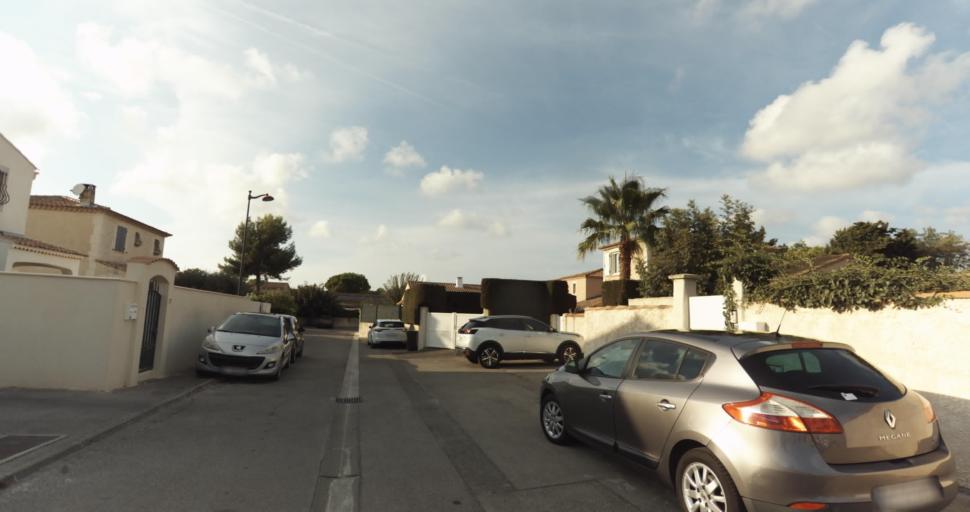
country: FR
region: Provence-Alpes-Cote d'Azur
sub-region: Departement des Bouches-du-Rhone
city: Saint-Victoret
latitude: 43.4153
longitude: 5.2346
